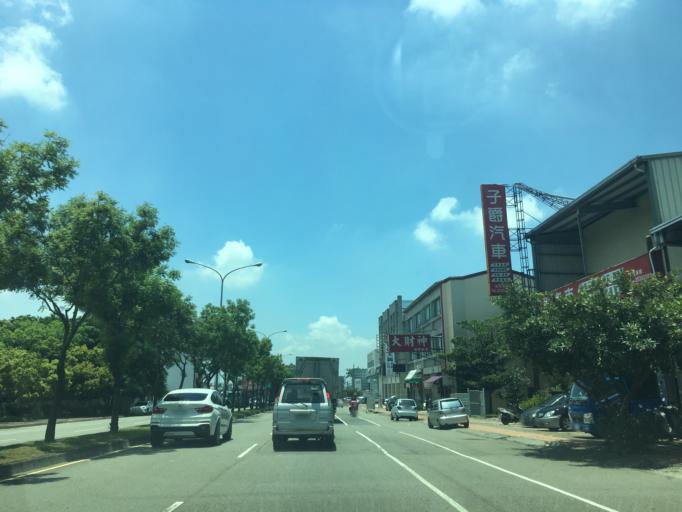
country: TW
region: Taiwan
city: Fengyuan
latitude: 24.2403
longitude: 120.7031
